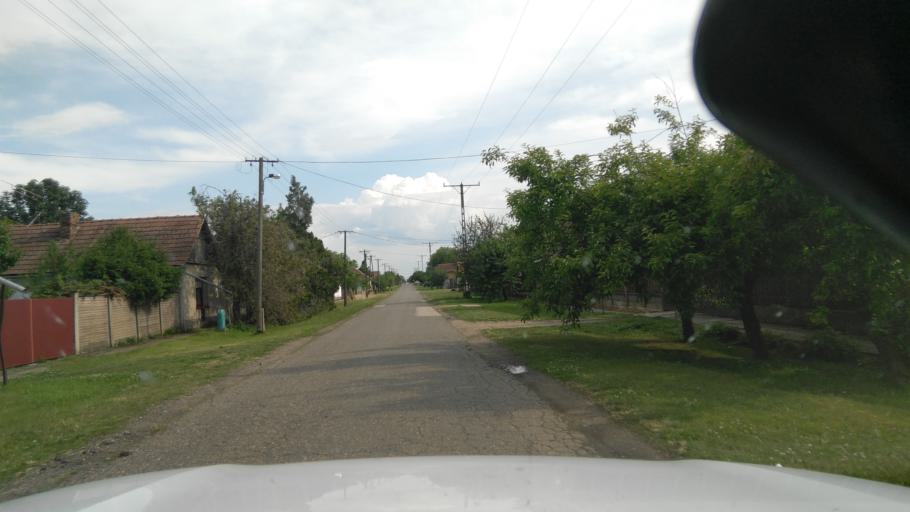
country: HU
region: Bekes
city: Ujkigyos
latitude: 46.5863
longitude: 21.0338
